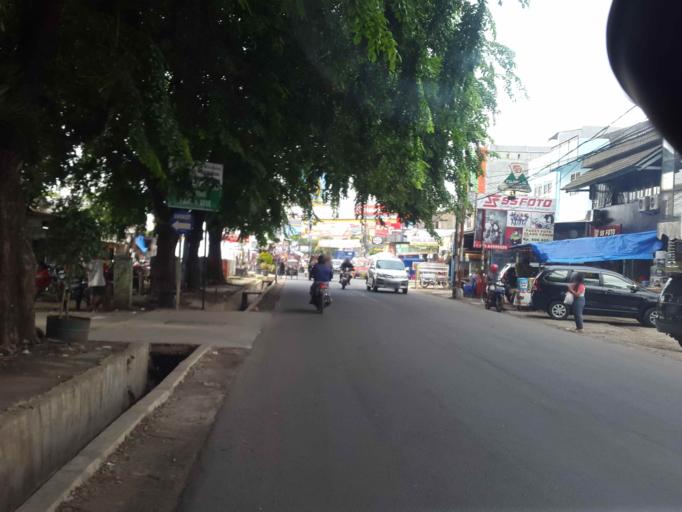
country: ID
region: West Java
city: Bekasi
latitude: -6.2863
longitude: 106.9134
